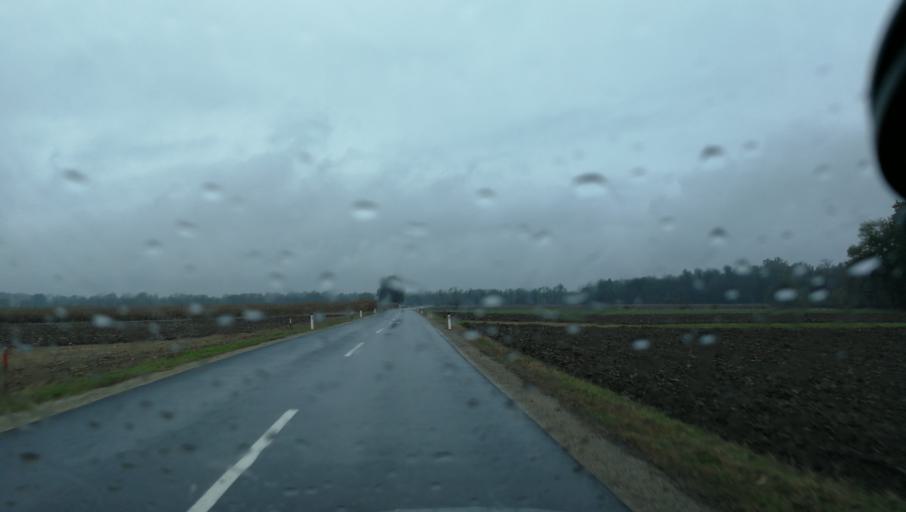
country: AT
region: Styria
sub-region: Politischer Bezirk Suedoststeiermark
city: Weinburg am Sassbach
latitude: 46.7331
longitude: 15.6977
